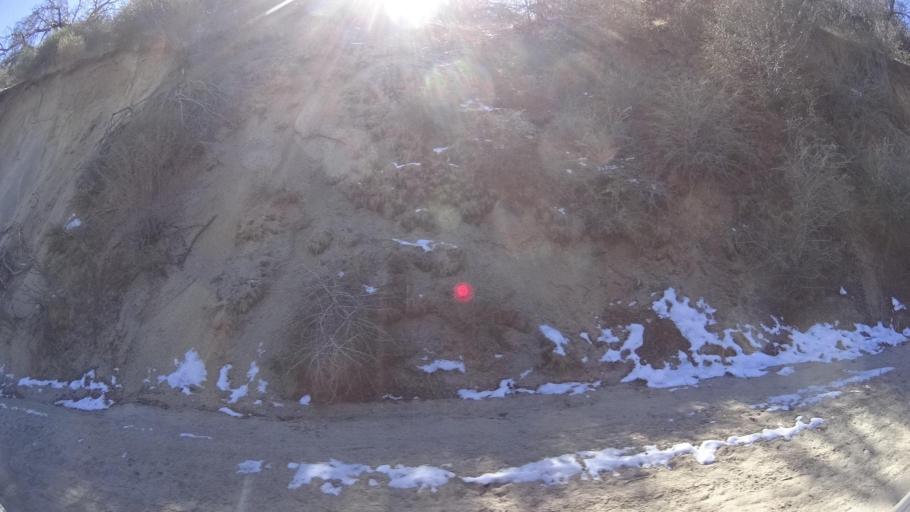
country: US
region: California
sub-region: Kern County
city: Alta Sierra
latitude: 35.7094
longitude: -118.5076
